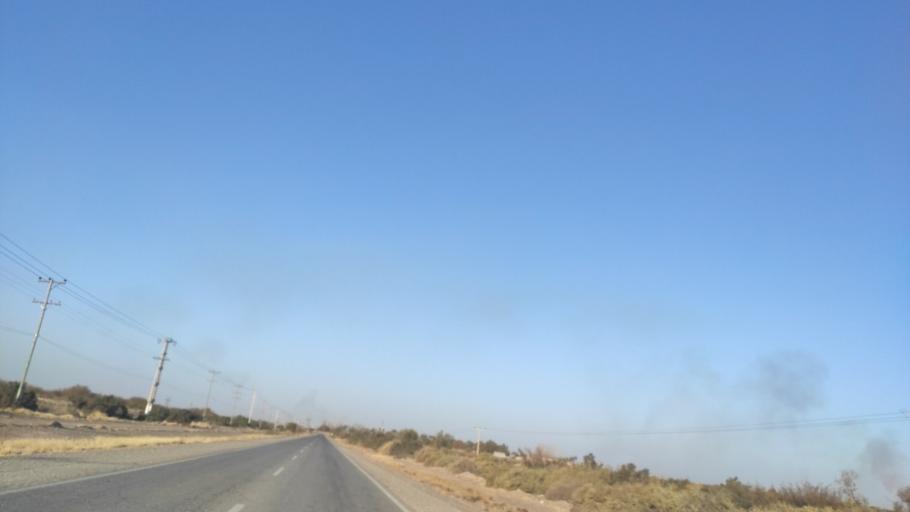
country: AR
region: San Juan
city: Villa Media Agua
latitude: -31.9790
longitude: -68.4707
